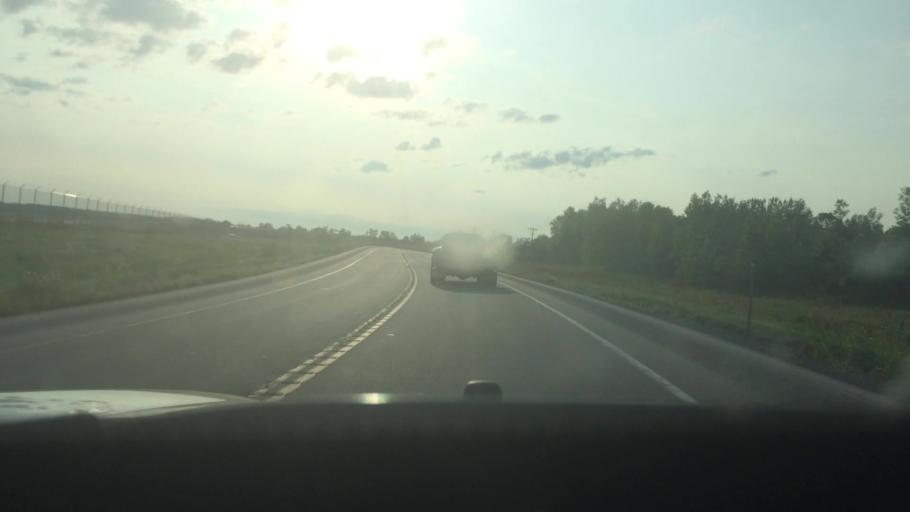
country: US
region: New York
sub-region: St. Lawrence County
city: Ogdensburg
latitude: 44.6860
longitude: -75.4498
